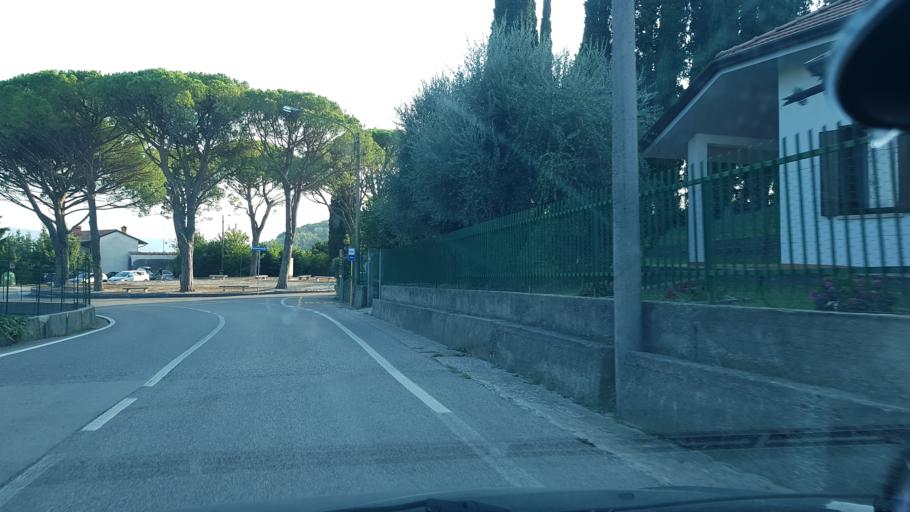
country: IT
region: Friuli Venezia Giulia
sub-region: Provincia di Gorizia
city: Gorizia
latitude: 45.9689
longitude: 13.6153
